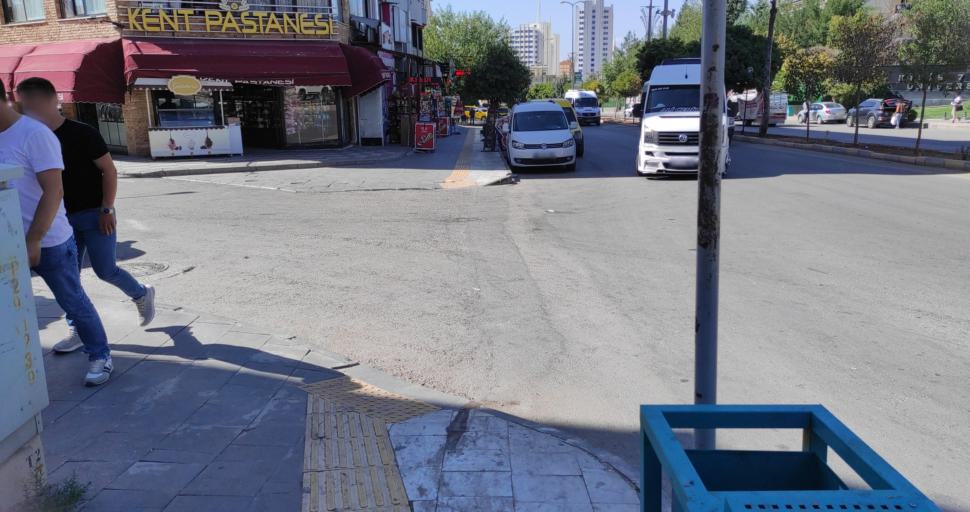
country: TR
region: Kilis
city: Kilis
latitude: 36.7281
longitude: 37.1001
